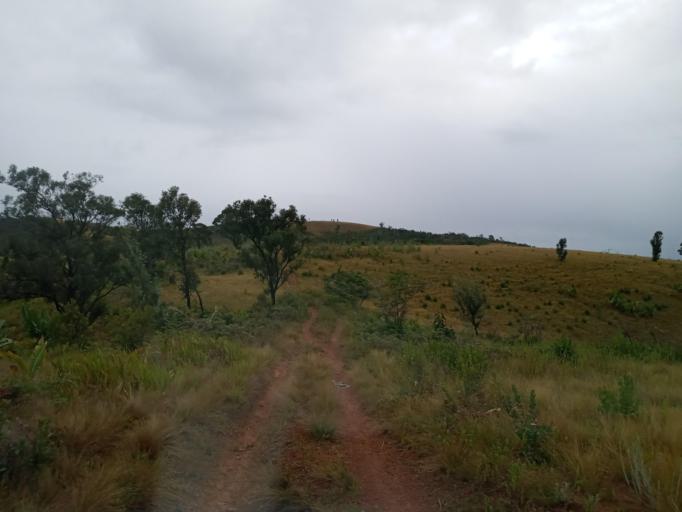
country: MG
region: Atsimo-Atsinanana
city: Vohipaho
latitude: -23.9921
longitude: 47.4019
